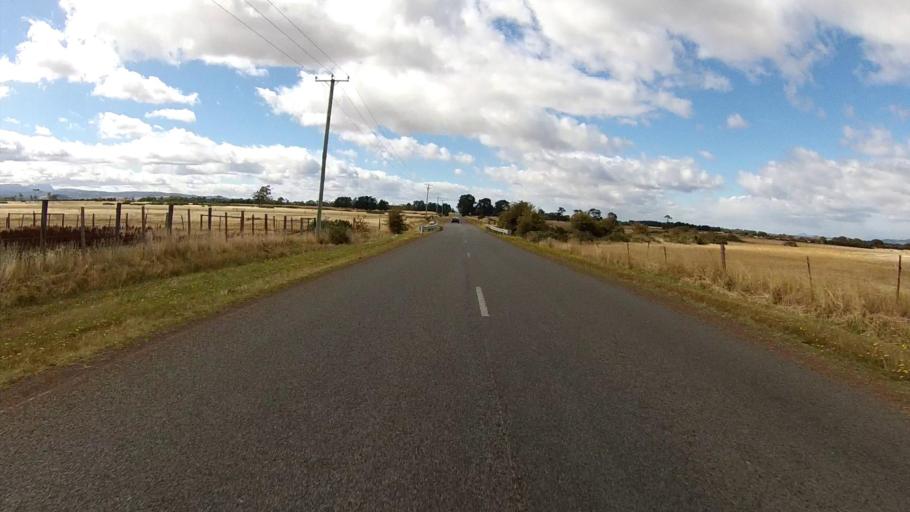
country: AU
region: Tasmania
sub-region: Northern Midlands
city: Evandale
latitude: -41.5988
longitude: 147.2740
